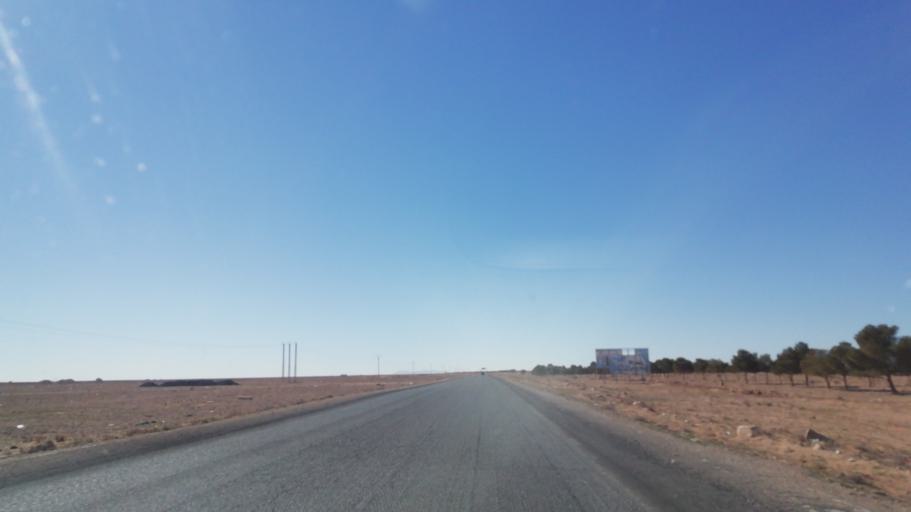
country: DZ
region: Saida
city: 'Ain el Hadjar
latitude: 34.0146
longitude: 0.0576
